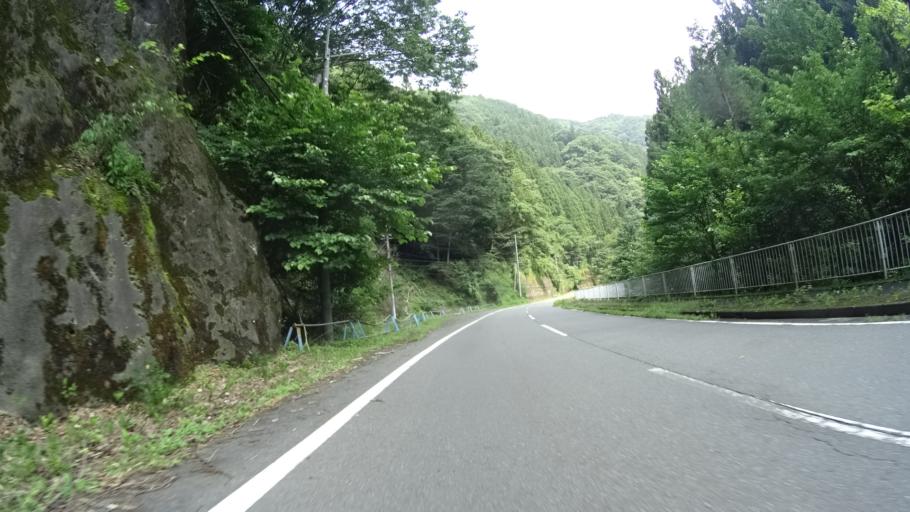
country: JP
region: Gunma
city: Tomioka
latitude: 36.0815
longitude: 138.8241
